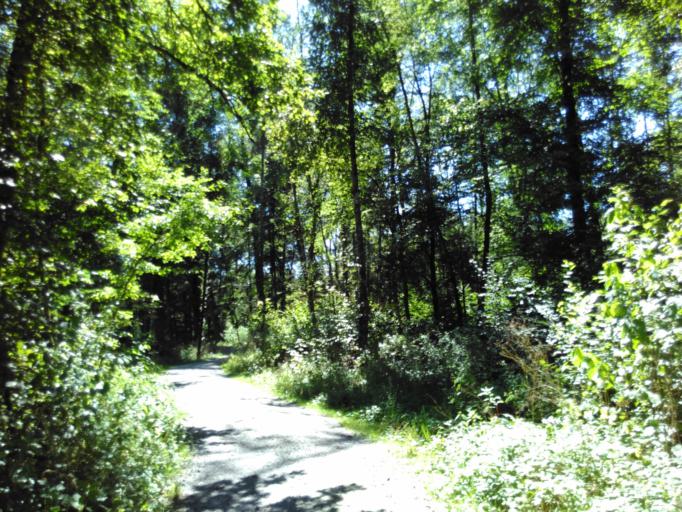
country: CH
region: Zurich
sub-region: Bezirk Hinwil
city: Rueti / Dorfzentrum, Suedl. Teil
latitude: 47.2481
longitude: 8.8526
